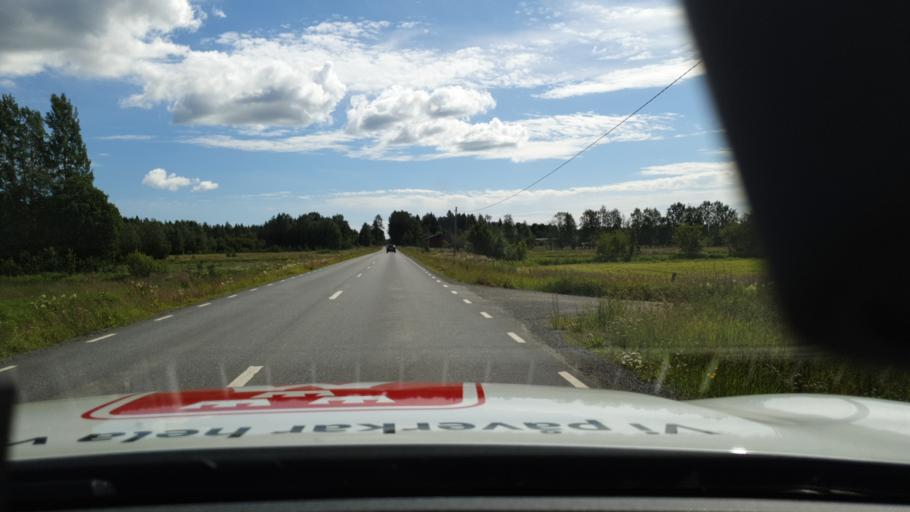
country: SE
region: Norrbotten
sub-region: Lulea Kommun
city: Gammelstad
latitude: 65.7950
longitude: 22.0705
